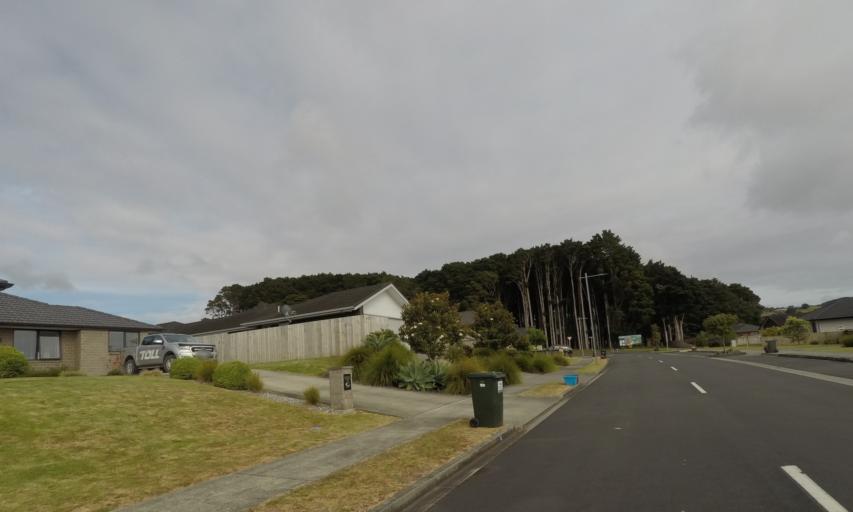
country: NZ
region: Northland
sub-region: Whangarei
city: Whangarei
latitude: -35.6759
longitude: 174.3169
